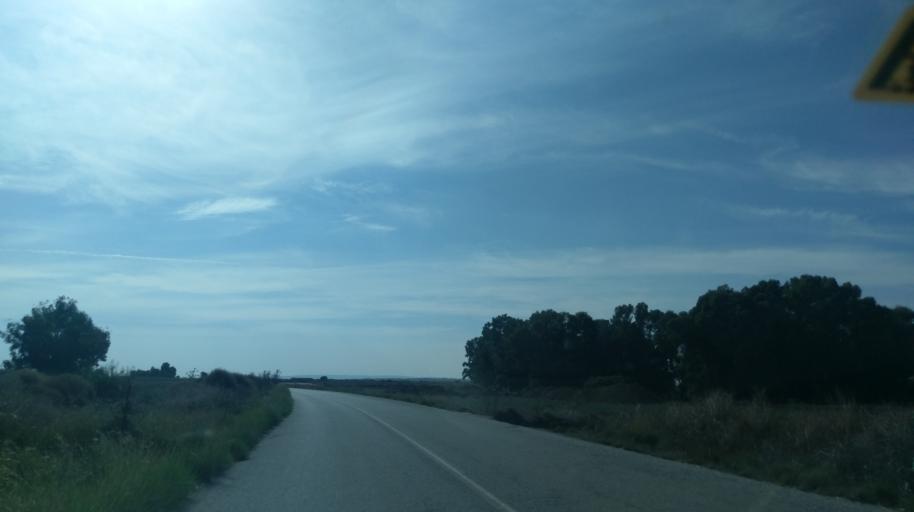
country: CY
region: Ammochostos
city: Lefkonoiko
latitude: 35.2039
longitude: 33.6949
